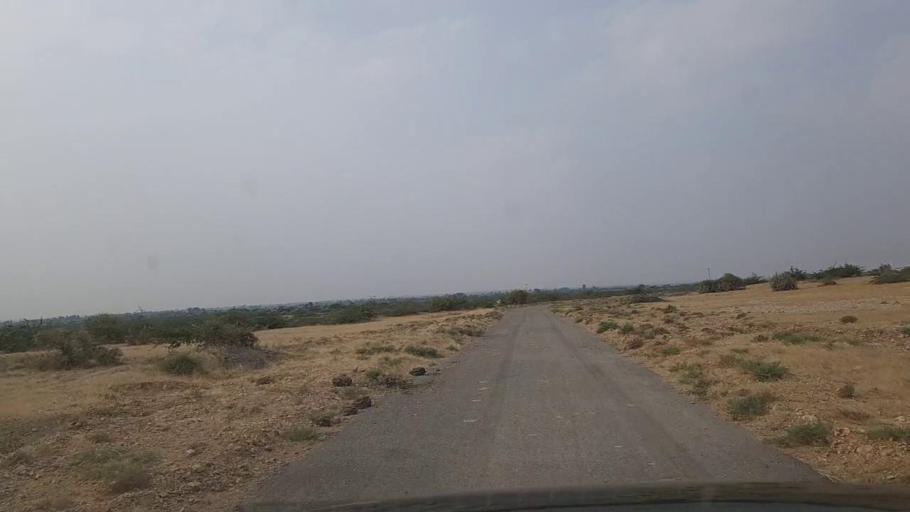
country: PK
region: Sindh
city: Thatta
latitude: 24.8049
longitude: 67.9157
